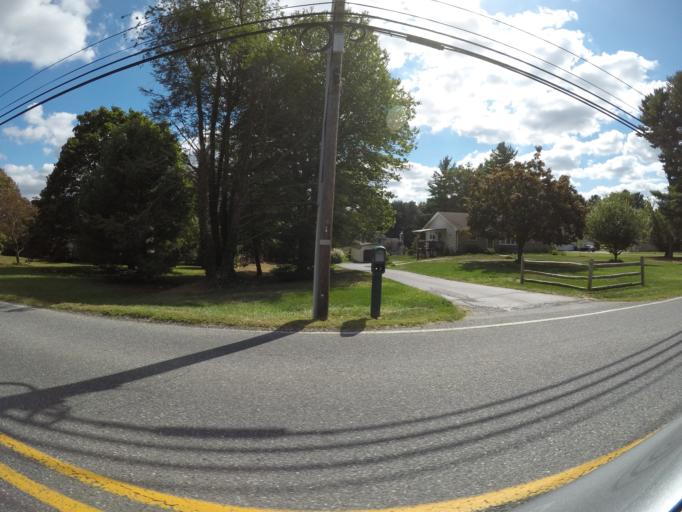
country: US
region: Maryland
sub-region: Harford County
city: Bel Air North
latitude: 39.5838
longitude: -76.3958
